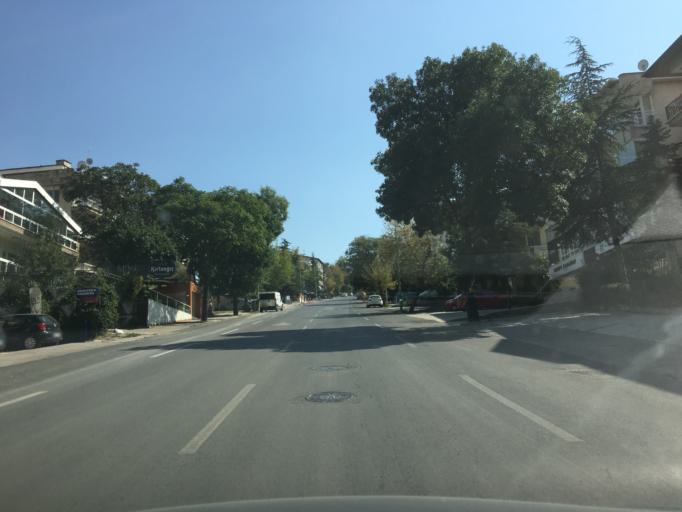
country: TR
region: Ankara
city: Cankaya
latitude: 39.8973
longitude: 32.8685
